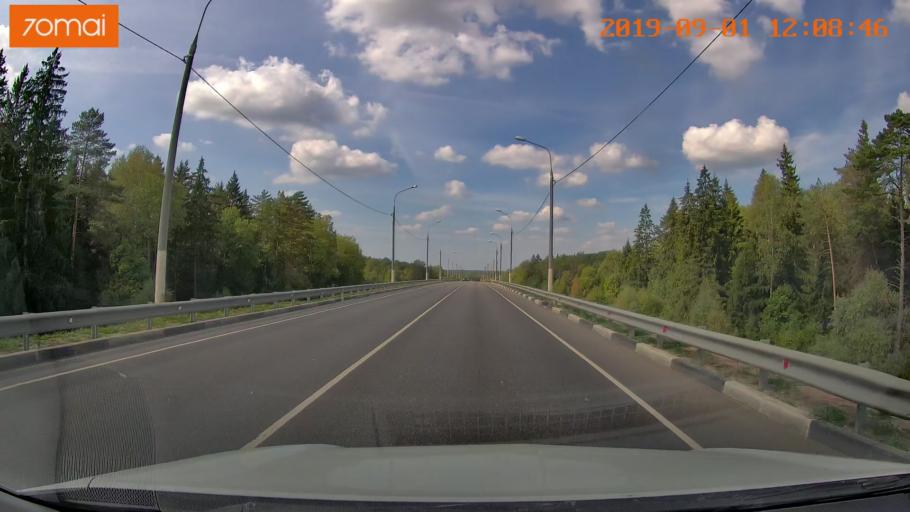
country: RU
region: Kaluga
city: Maloyaroslavets
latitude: 54.9787
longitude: 36.4371
